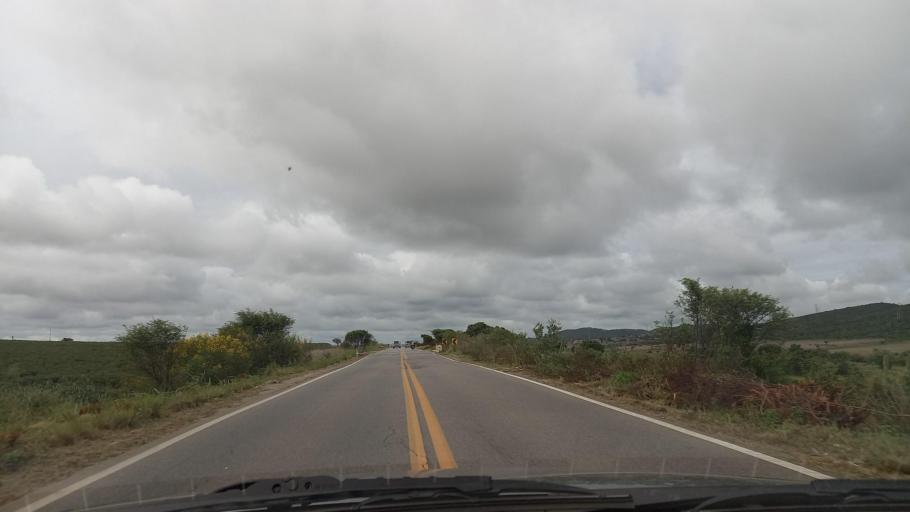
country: BR
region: Pernambuco
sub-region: Sao Joao
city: Sao Joao
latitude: -8.8781
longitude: -36.3959
